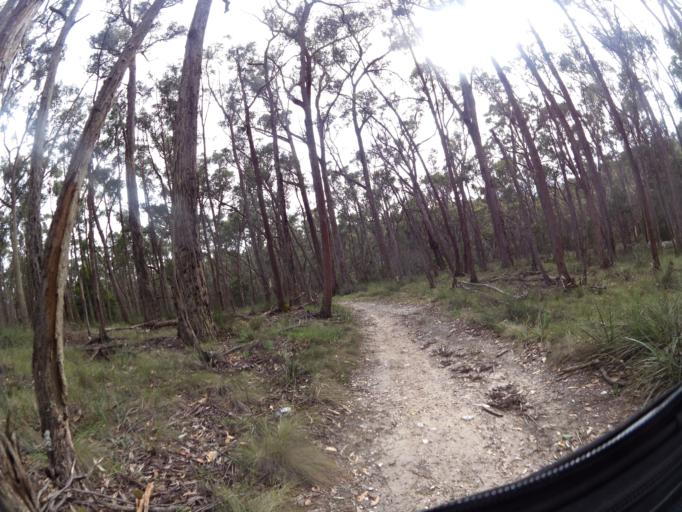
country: AU
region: Victoria
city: Brown Hill
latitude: -37.4752
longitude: 143.9123
